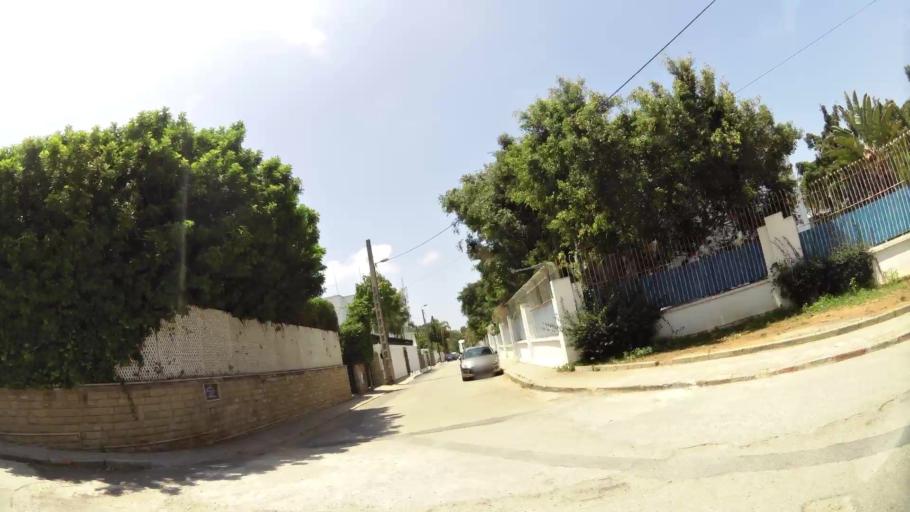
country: MA
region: Rabat-Sale-Zemmour-Zaer
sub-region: Rabat
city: Rabat
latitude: 34.0145
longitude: -6.8219
